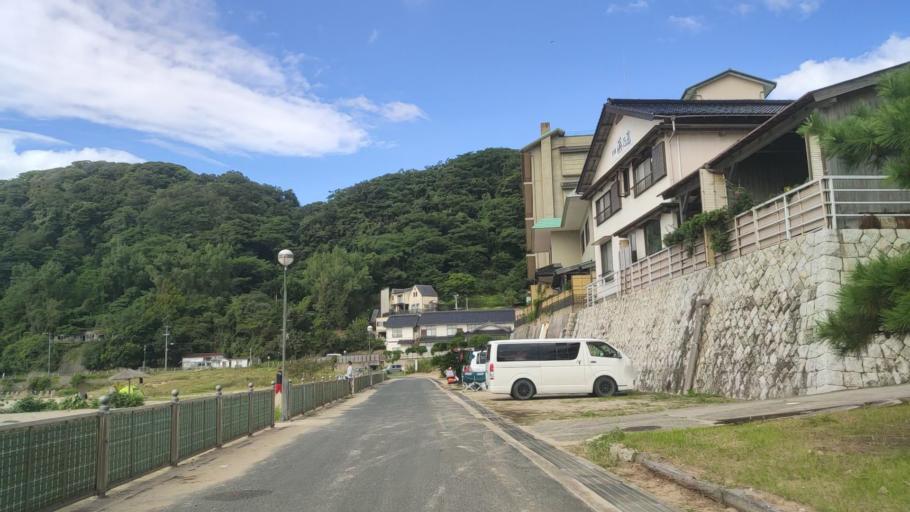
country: JP
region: Hyogo
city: Toyooka
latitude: 35.6678
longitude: 134.9678
